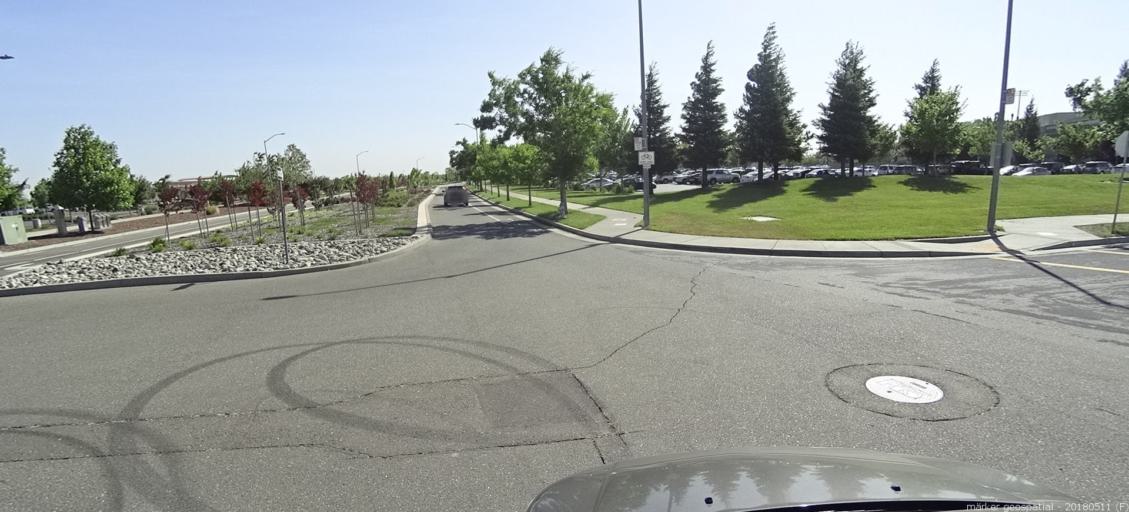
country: US
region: California
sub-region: Sacramento County
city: Rio Linda
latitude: 38.6593
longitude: -121.5189
